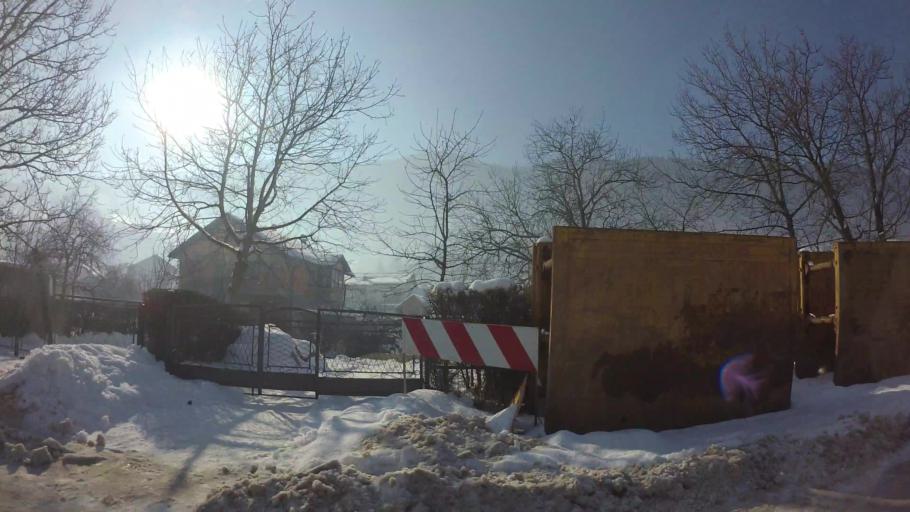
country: BA
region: Federation of Bosnia and Herzegovina
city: Gracanica
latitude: 43.7992
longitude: 18.3061
